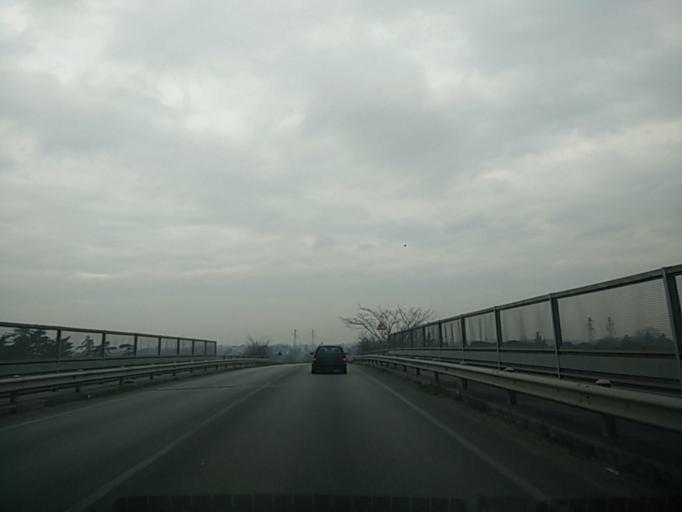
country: IT
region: Emilia-Romagna
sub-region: Provincia di Rimini
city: Santarcangelo
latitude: 44.0703
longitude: 12.4609
